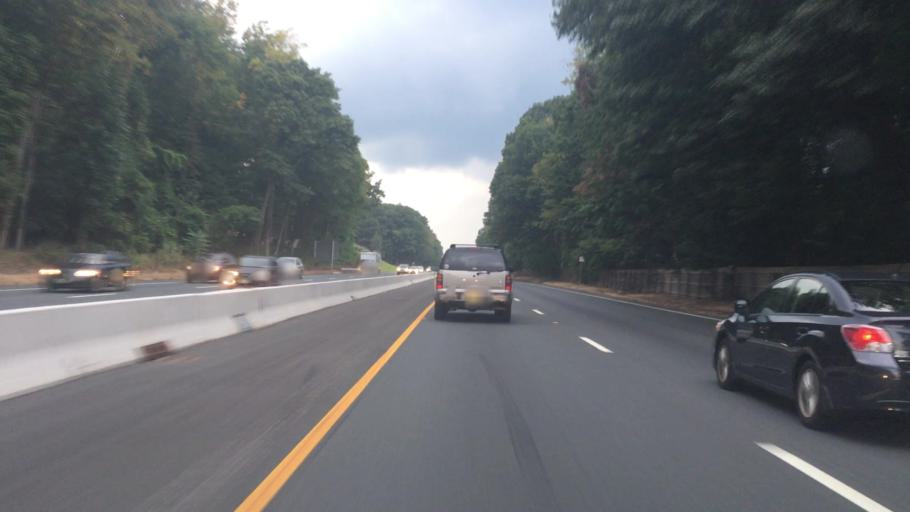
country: US
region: New Jersey
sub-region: Bergen County
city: Wyckoff
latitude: 41.0002
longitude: -74.1837
